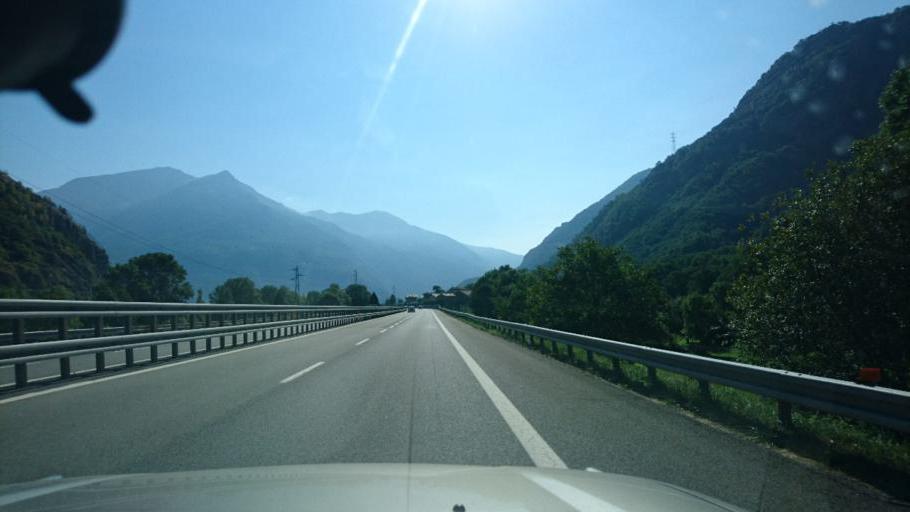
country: IT
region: Aosta Valley
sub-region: Valle d'Aosta
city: Bard
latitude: 45.6020
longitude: 7.7520
